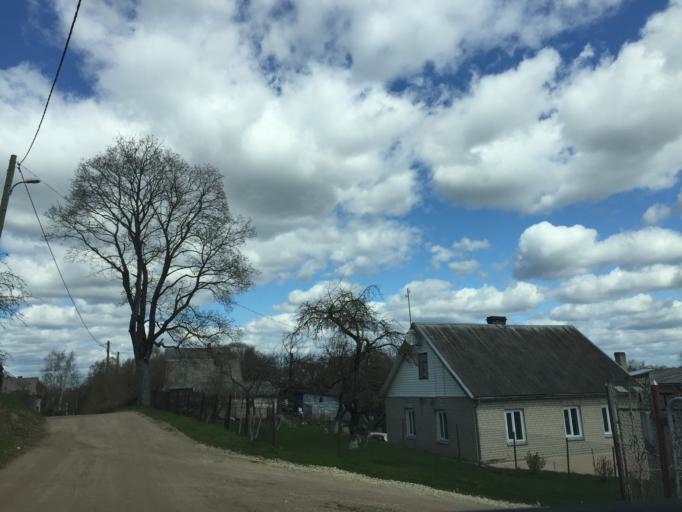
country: LV
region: Rezekne
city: Rezekne
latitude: 56.4903
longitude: 27.3294
